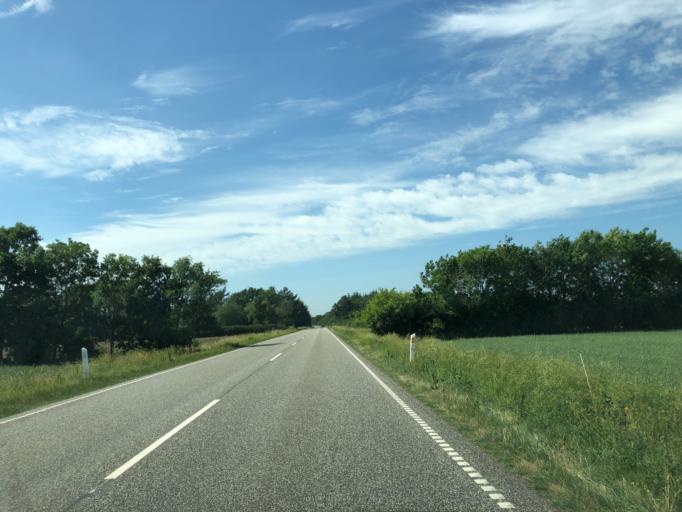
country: DK
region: Central Jutland
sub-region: Ikast-Brande Kommune
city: Brande
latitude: 55.9095
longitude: 9.1866
